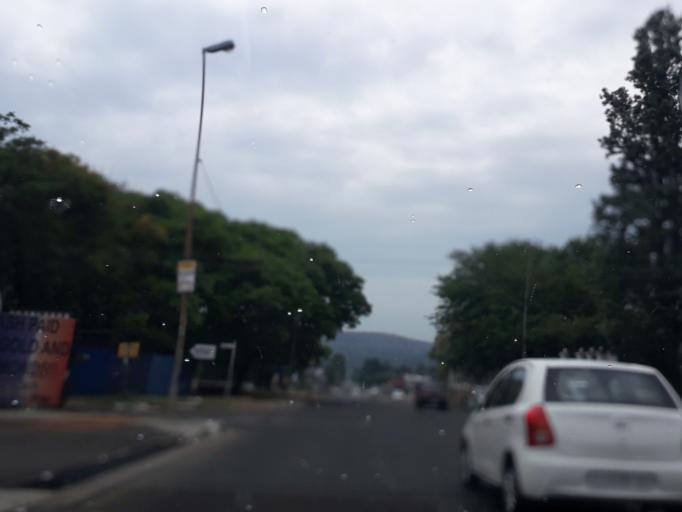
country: ZA
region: Gauteng
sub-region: City of Johannesburg Metropolitan Municipality
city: Johannesburg
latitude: -26.1055
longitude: 27.9793
